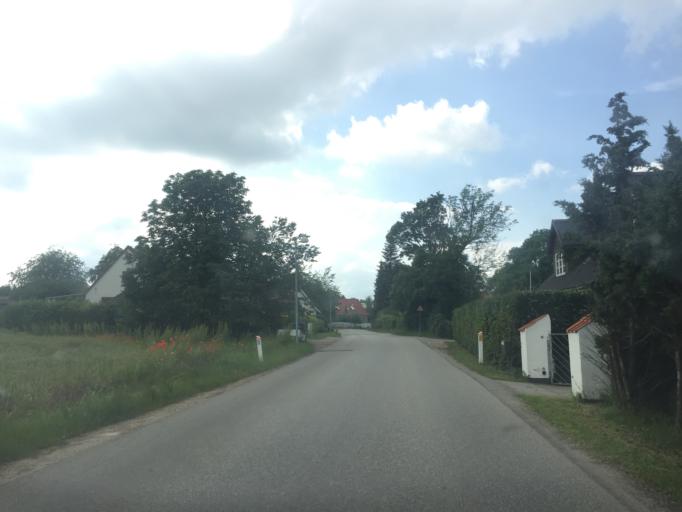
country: DK
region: Capital Region
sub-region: Hoje-Taastrup Kommune
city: Flong
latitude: 55.6916
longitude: 12.1673
